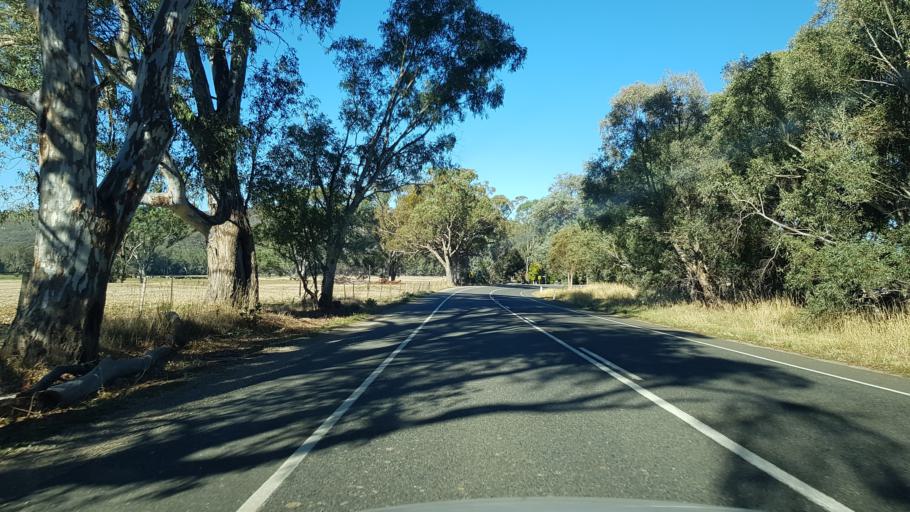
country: AU
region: Victoria
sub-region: Wangaratta
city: Wangaratta
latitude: -36.6099
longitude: 146.3932
